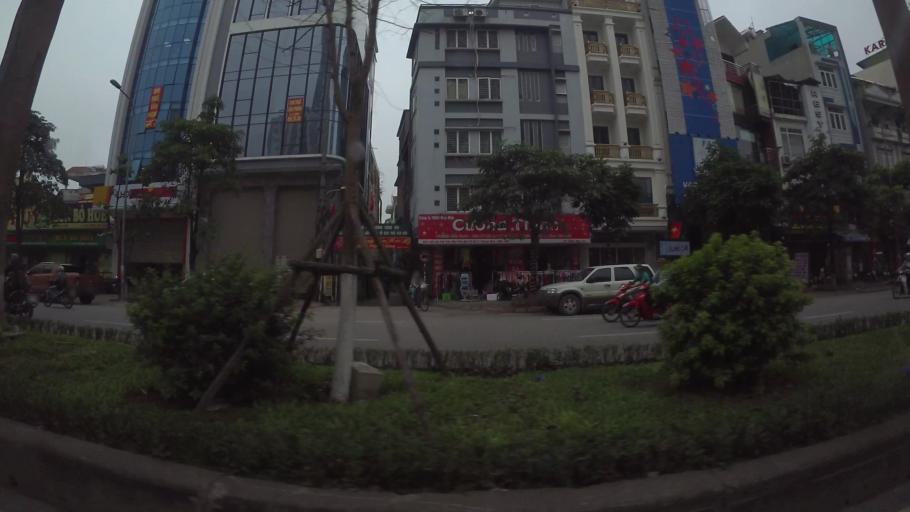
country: VN
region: Ha Noi
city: Hai BaTrung
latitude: 20.9834
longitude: 105.8524
